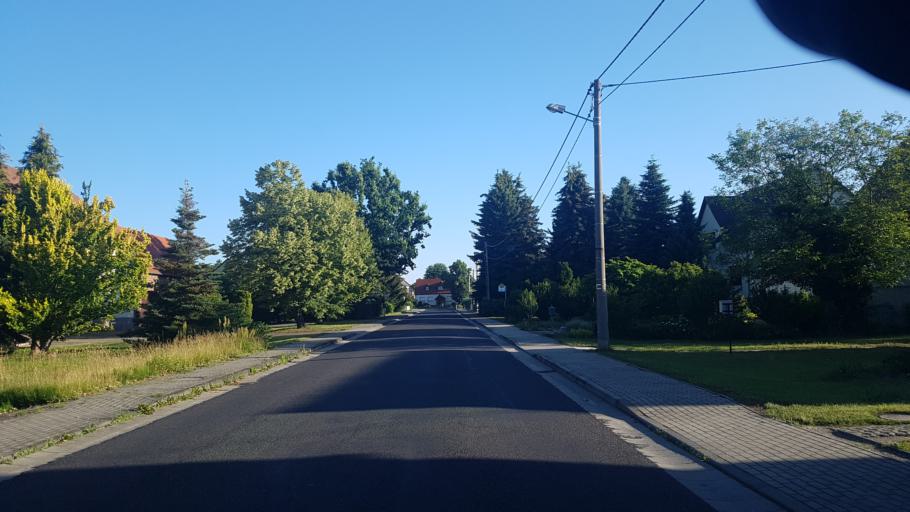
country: DE
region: Brandenburg
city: Schilda
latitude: 51.5880
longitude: 13.3839
